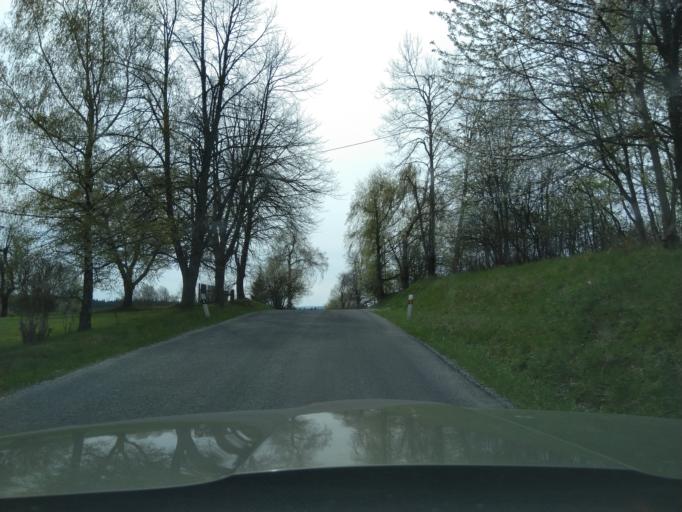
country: CZ
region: Jihocesky
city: Vacov
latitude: 49.1659
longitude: 13.6829
